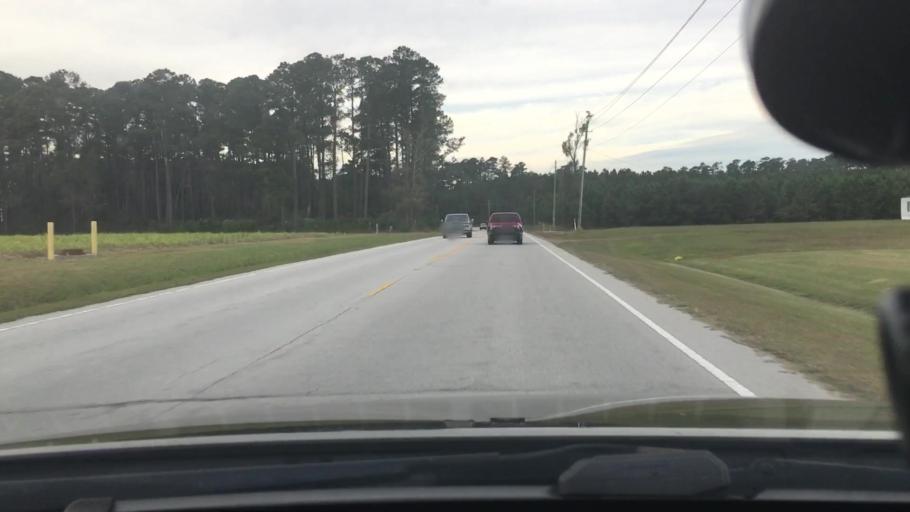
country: US
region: North Carolina
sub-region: Pitt County
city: Windsor
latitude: 35.4671
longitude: -77.2775
